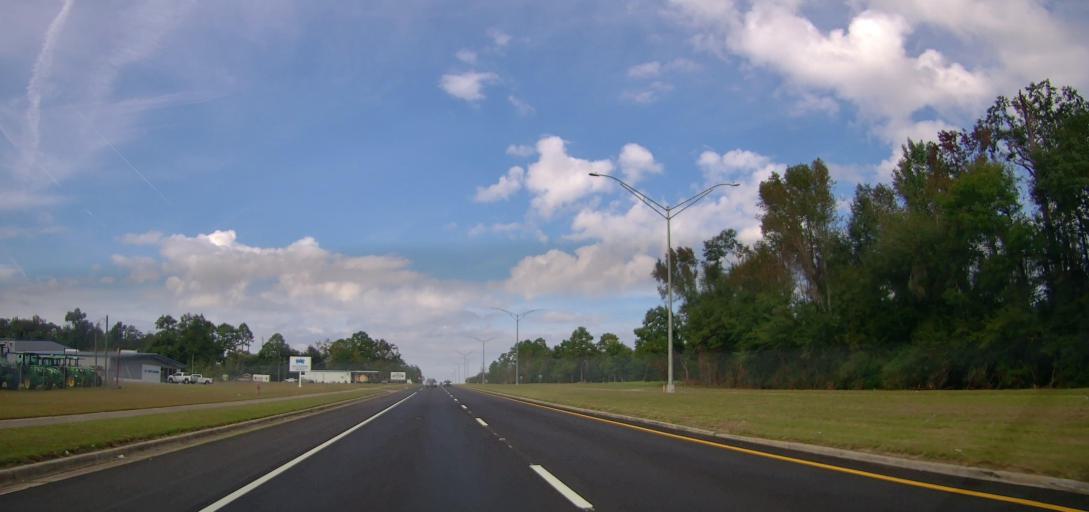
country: US
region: Georgia
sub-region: Mitchell County
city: Pelham
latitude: 31.1255
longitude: -84.1403
